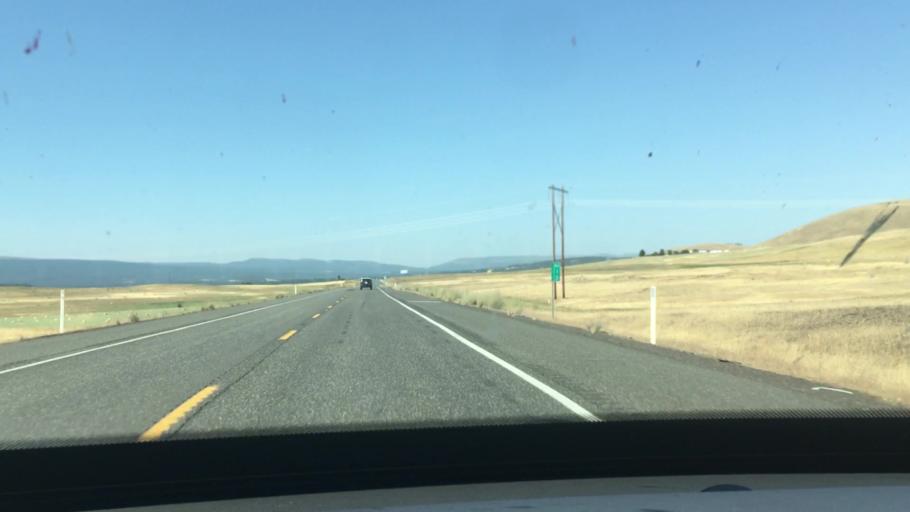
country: US
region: Washington
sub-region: Klickitat County
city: Goldendale
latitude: 45.7900
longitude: -120.8212
